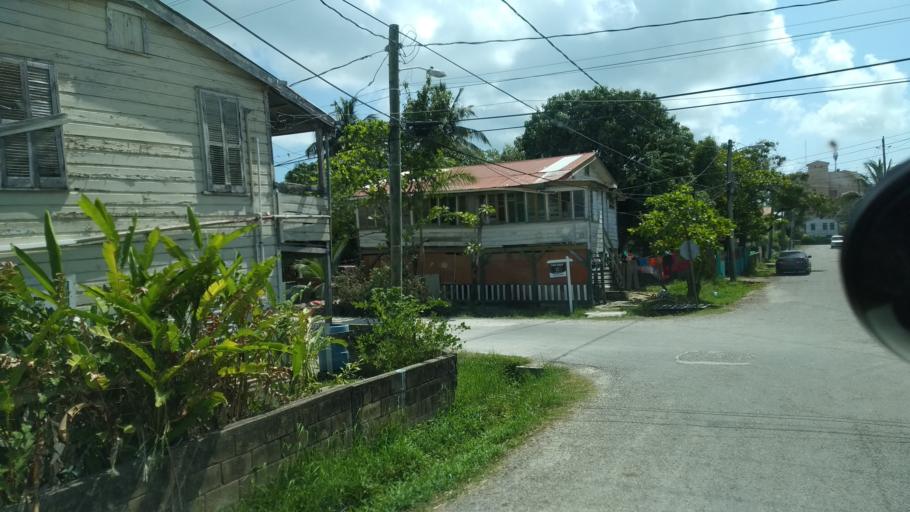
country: BZ
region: Belize
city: Belize City
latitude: 17.5071
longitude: -88.1928
